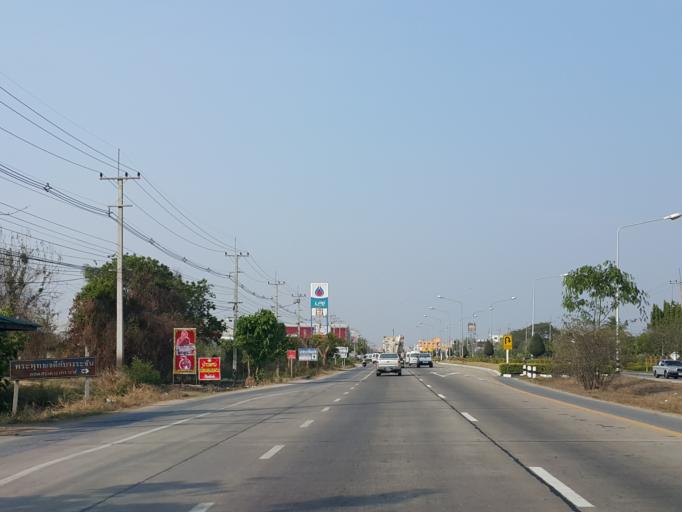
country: TH
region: Suphan Buri
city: Doembang Nangbuat
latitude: 14.7991
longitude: 100.1087
